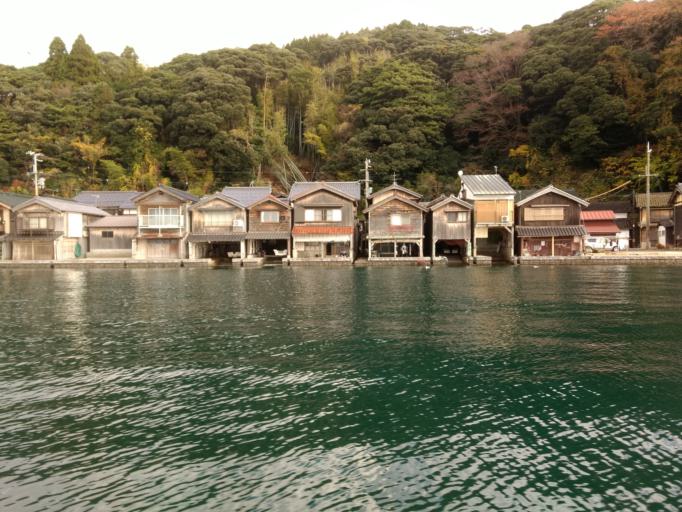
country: JP
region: Kyoto
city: Miyazu
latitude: 35.6742
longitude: 135.2895
